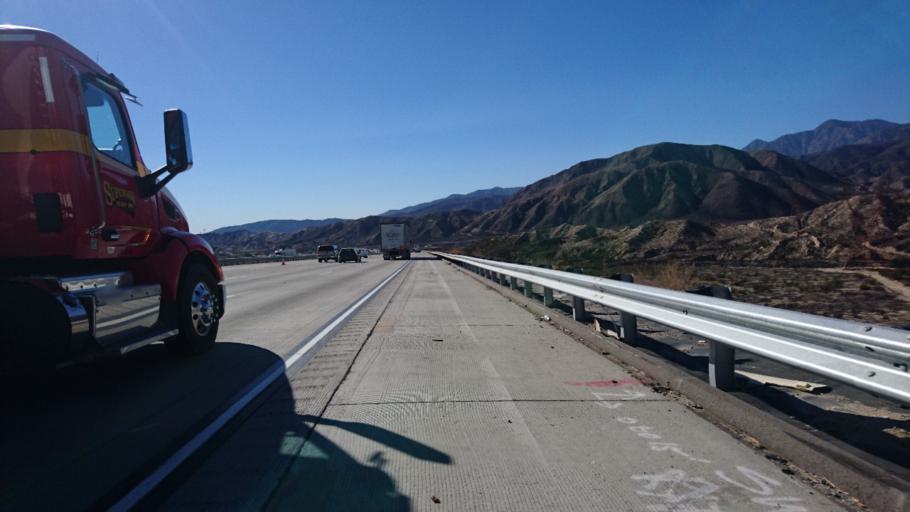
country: US
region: California
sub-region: San Bernardino County
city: Oak Hills
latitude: 34.3289
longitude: -117.4826
